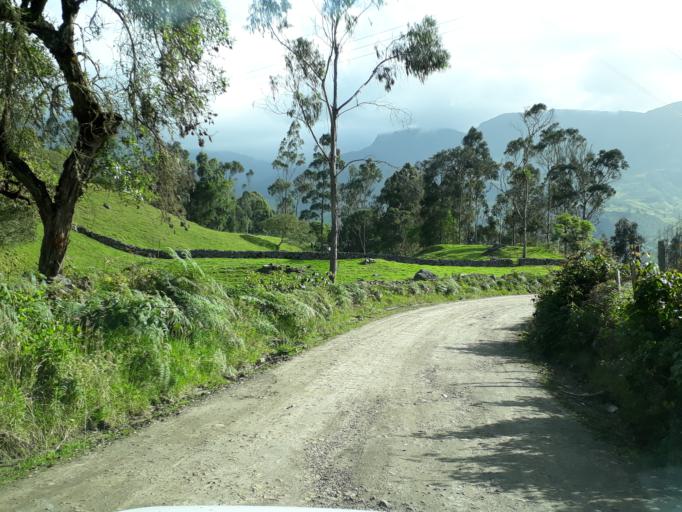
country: CO
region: Cundinamarca
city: Junin
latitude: 4.7841
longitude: -73.6825
